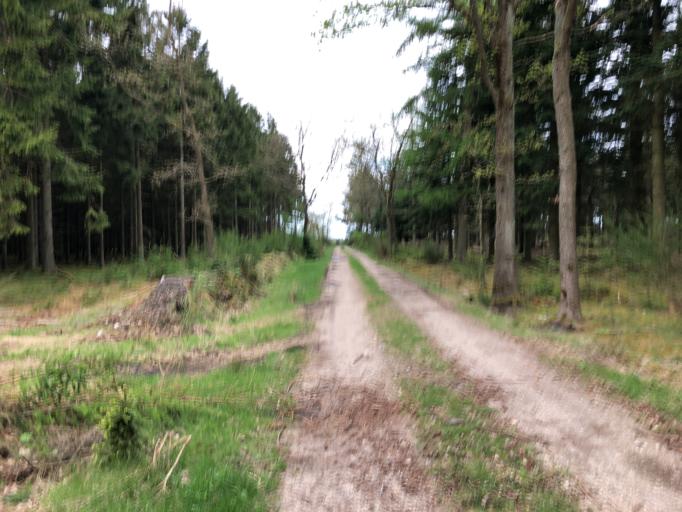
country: DK
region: Central Jutland
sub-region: Holstebro Kommune
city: Ulfborg
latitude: 56.2934
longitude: 8.4260
